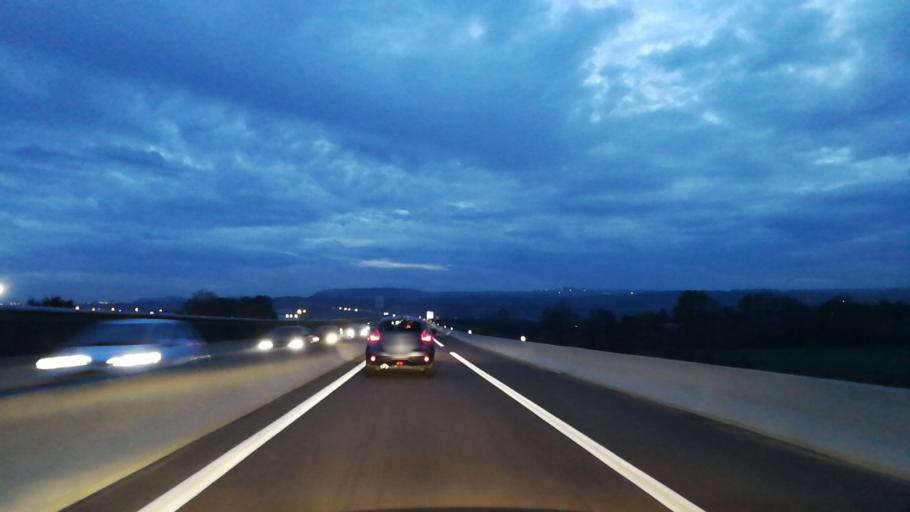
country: FR
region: Bourgogne
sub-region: Departement de la Cote-d'Or
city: Ahuy
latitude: 47.3587
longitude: 5.0386
